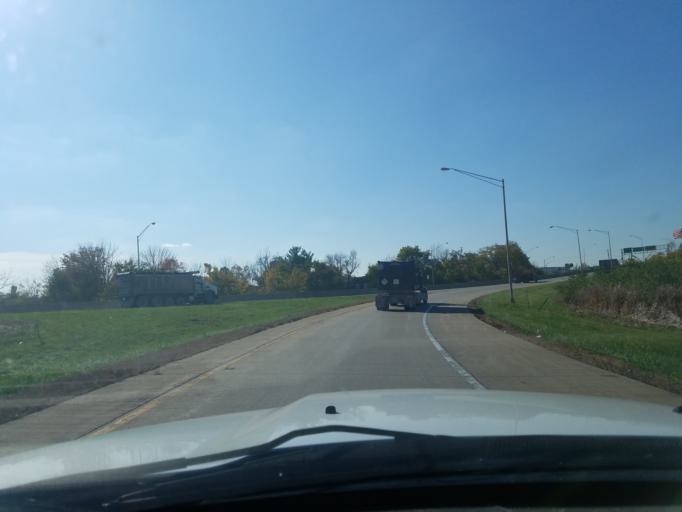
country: US
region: Indiana
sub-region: Marion County
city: Speedway
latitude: 39.7316
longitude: -86.2447
